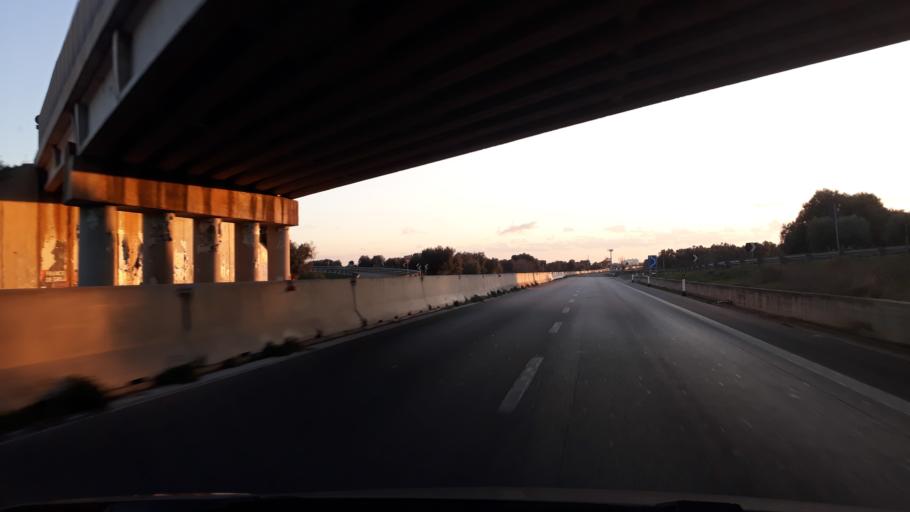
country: IT
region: Apulia
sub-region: Provincia di Brindisi
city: Pezze di Greco
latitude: 40.8330
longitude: 17.4477
